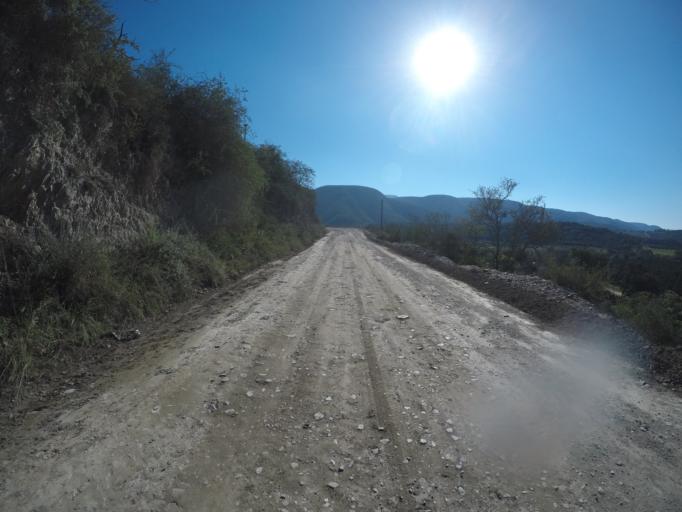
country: ZA
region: Eastern Cape
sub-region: Cacadu District Municipality
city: Kruisfontein
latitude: -33.6651
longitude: 24.5678
